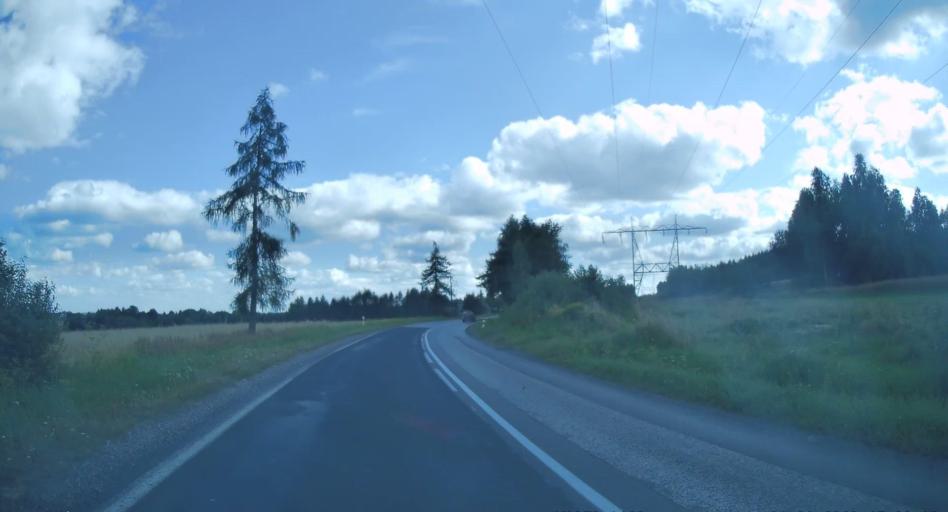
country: PL
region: Swietokrzyskie
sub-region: Powiat kielecki
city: Lagow
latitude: 50.8115
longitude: 21.0796
